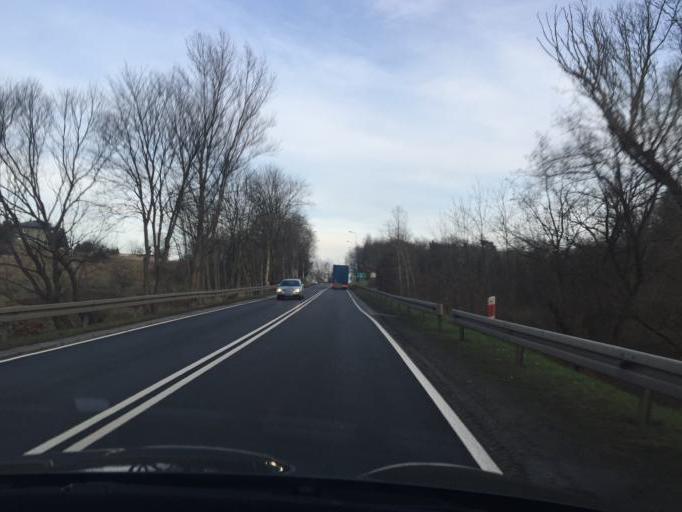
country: PL
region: Lubusz
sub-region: Powiat zielonogorski
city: Nowogrod Bobrzanski
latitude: 51.7969
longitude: 15.2442
